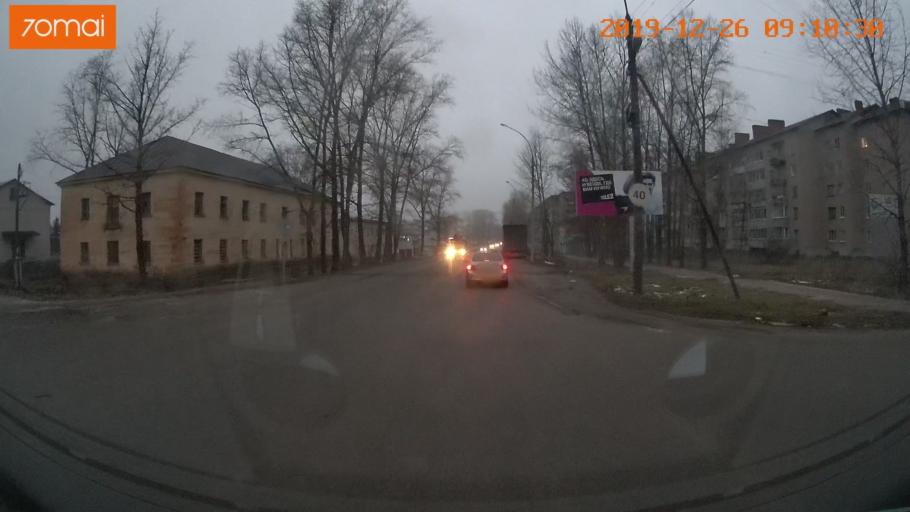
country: RU
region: Vologda
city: Gryazovets
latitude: 58.8714
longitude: 40.2526
